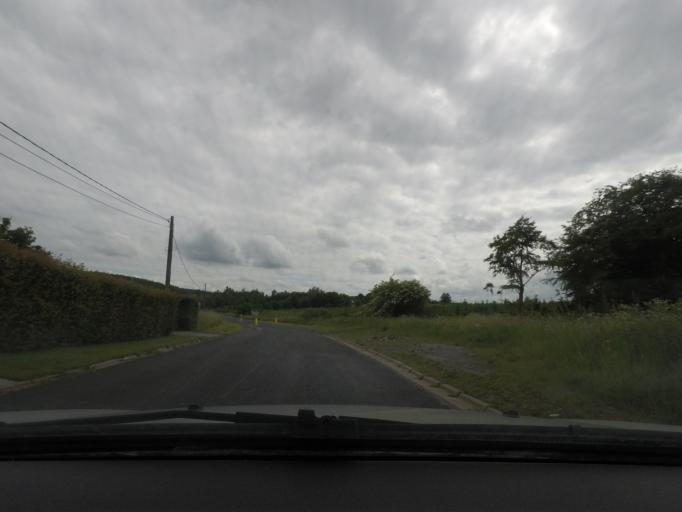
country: BE
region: Wallonia
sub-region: Province du Luxembourg
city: Leglise
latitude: 49.8119
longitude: 5.5405
